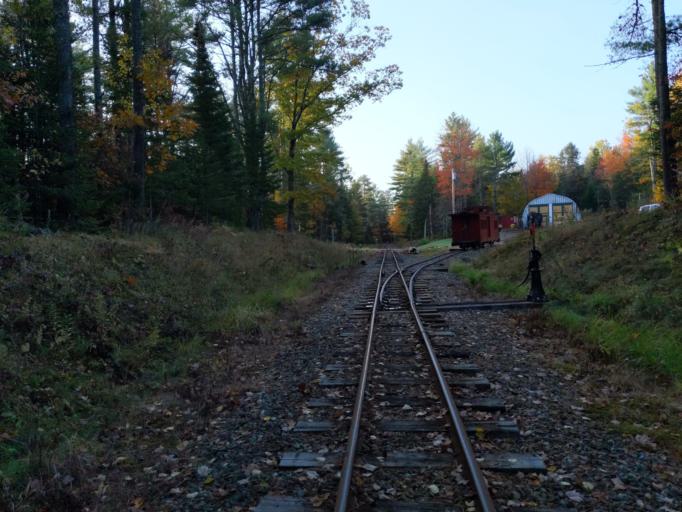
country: US
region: Maine
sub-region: Lincoln County
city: Wiscasset
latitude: 44.0728
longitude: -69.6215
